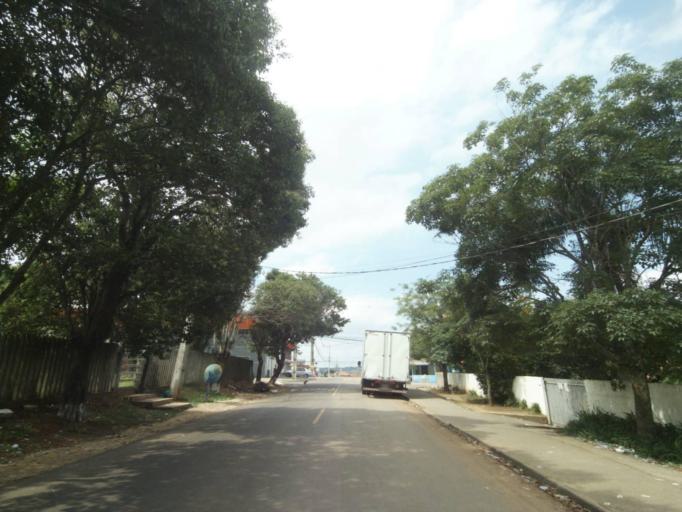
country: BR
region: Parana
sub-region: Curitiba
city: Curitiba
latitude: -25.5015
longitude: -49.3485
